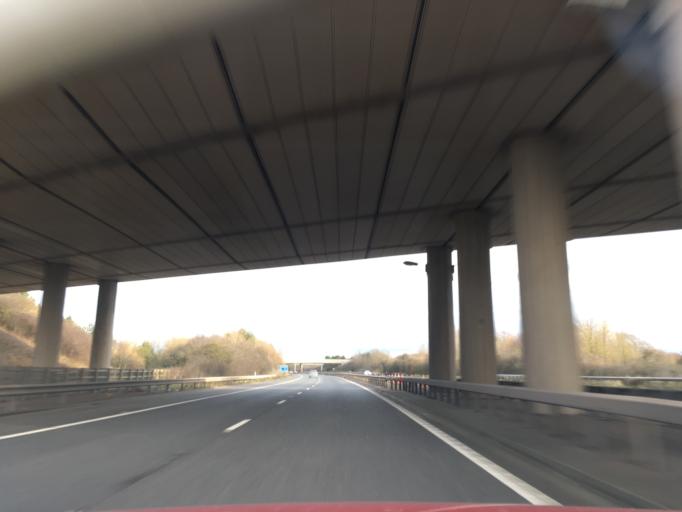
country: GB
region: England
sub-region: South Gloucestershire
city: Severn Beach
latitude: 51.5691
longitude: -2.6428
